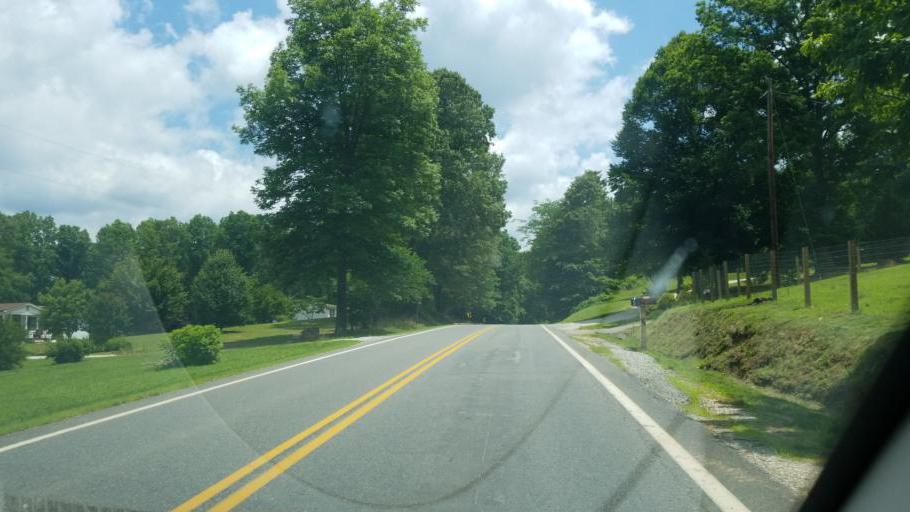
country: US
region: Virginia
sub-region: Amherst County
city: Amherst
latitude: 37.5615
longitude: -78.9793
